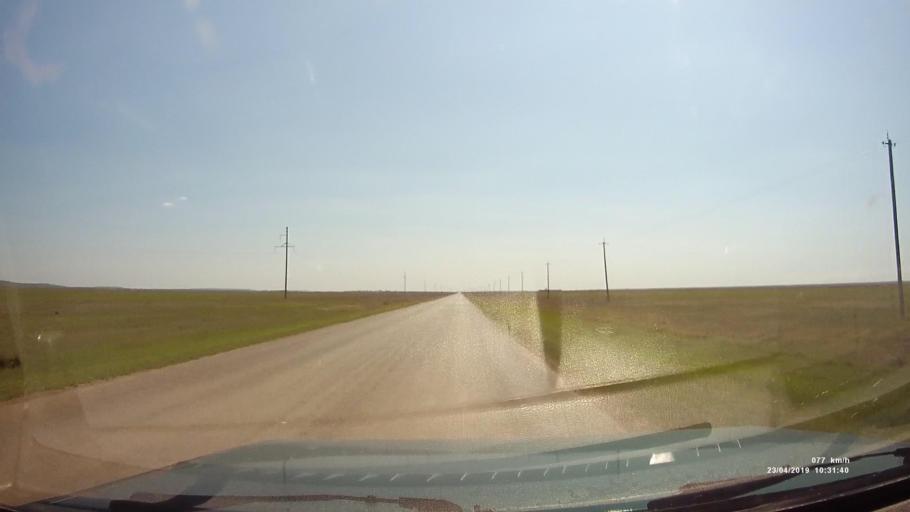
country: RU
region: Kalmykiya
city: Yashalta
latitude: 46.5848
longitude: 42.5651
